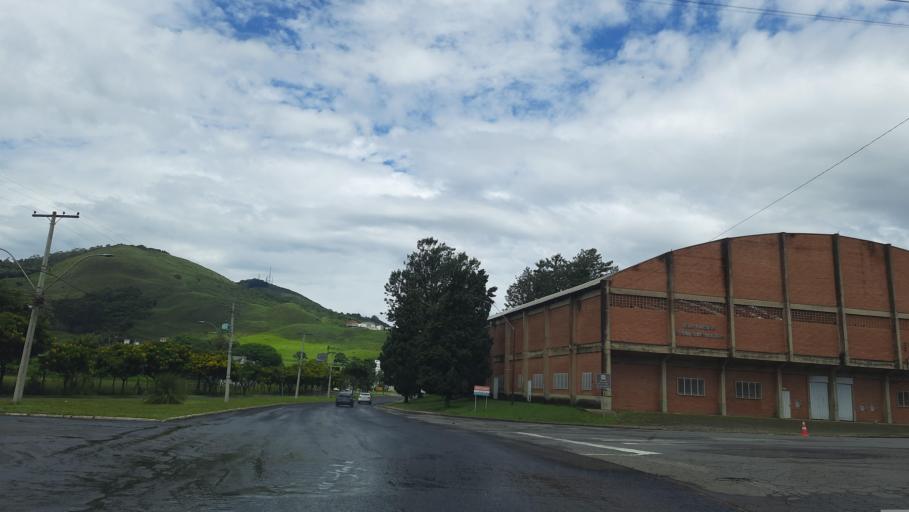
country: BR
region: Minas Gerais
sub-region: Pocos De Caldas
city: Pocos de Caldas
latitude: -21.7760
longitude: -46.6060
